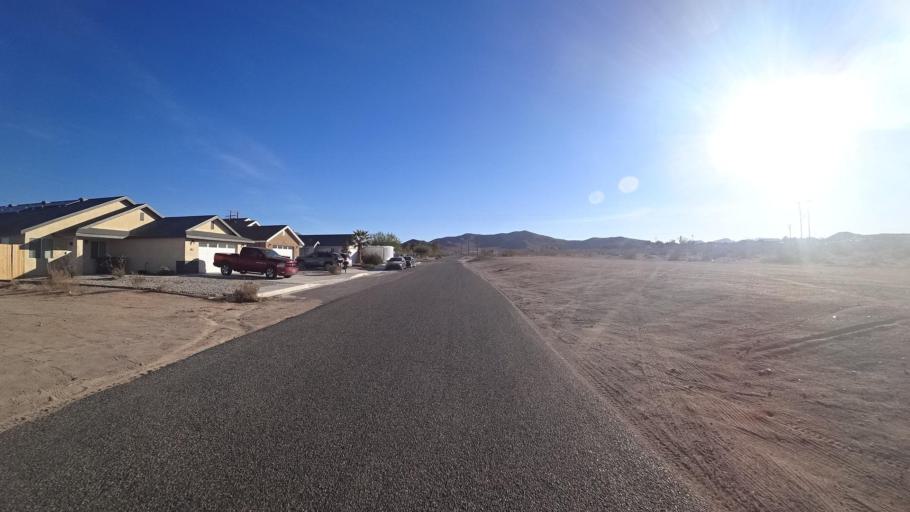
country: US
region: California
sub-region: Kern County
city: Ridgecrest
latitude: 35.5944
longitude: -117.6971
